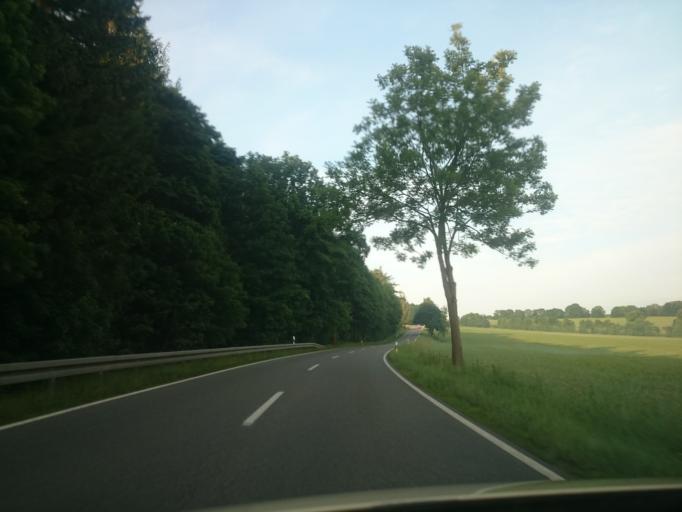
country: DE
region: Saxony
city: Grosshartmannsdorf
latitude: 50.7508
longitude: 13.2985
